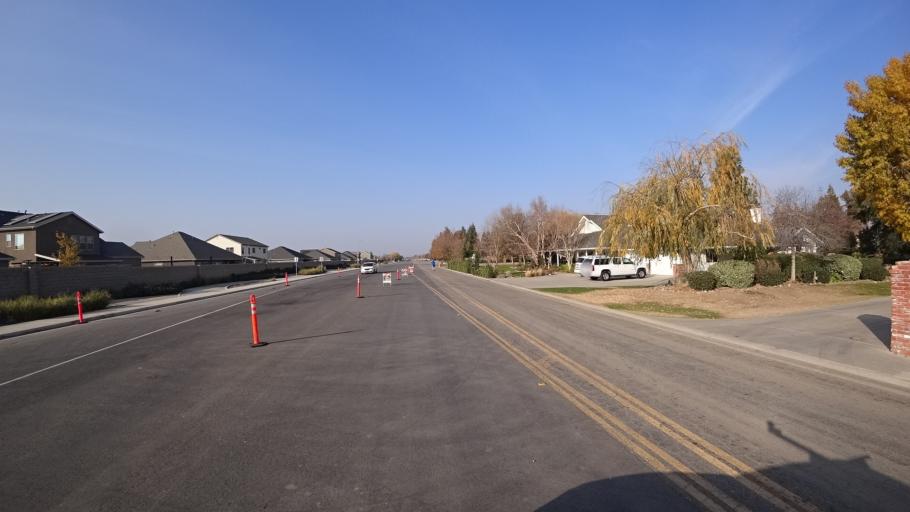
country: US
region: California
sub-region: Kern County
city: Greenacres
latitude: 35.4343
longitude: -119.1063
